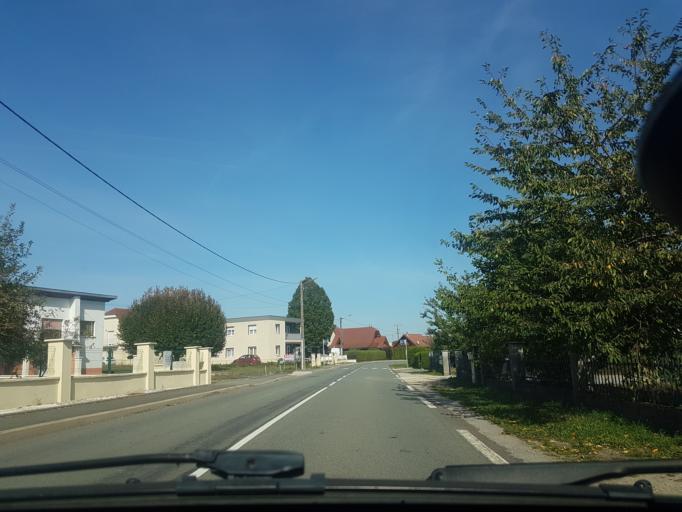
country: FR
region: Franche-Comte
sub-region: Territoire de Belfort
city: Offemont
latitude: 47.6590
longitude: 6.9068
